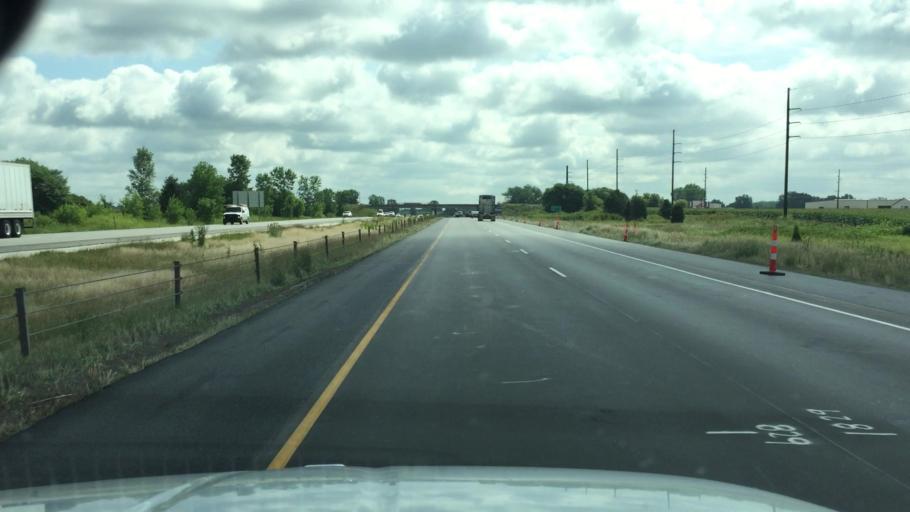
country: US
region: Iowa
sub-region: Scott County
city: Eldridge
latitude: 41.5997
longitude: -90.6034
